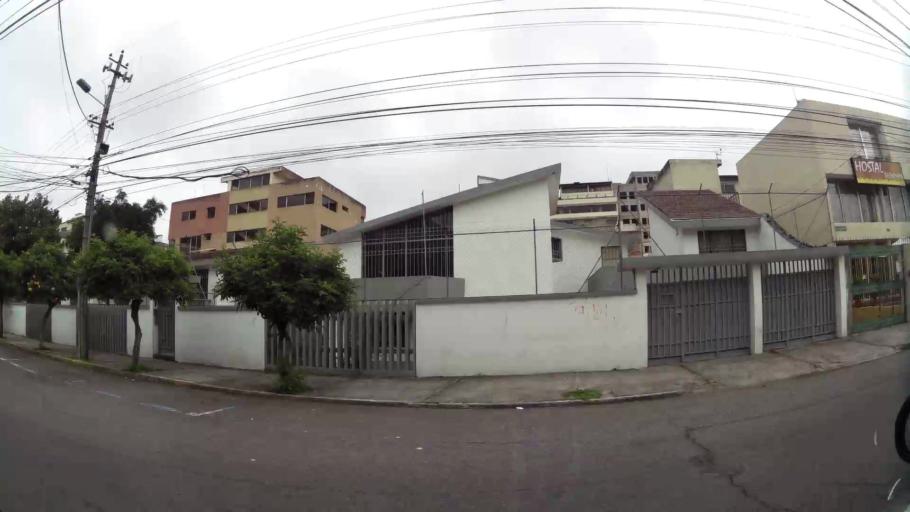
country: EC
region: Pichincha
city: Quito
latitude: -0.1931
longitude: -78.4927
